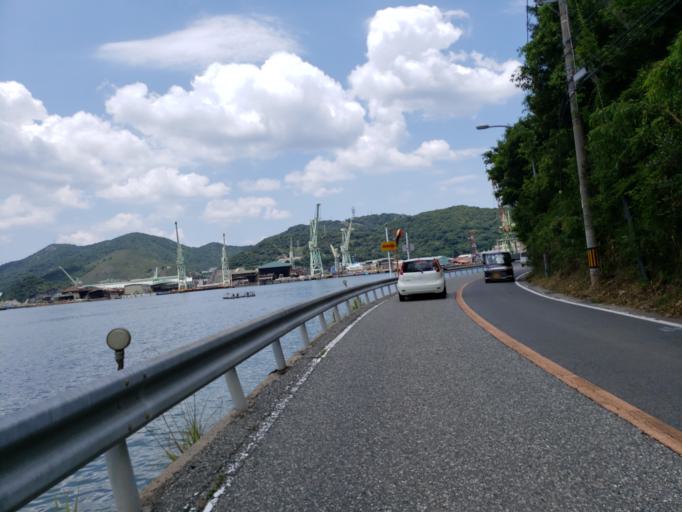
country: JP
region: Hyogo
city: Aioi
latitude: 34.7885
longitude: 134.4728
